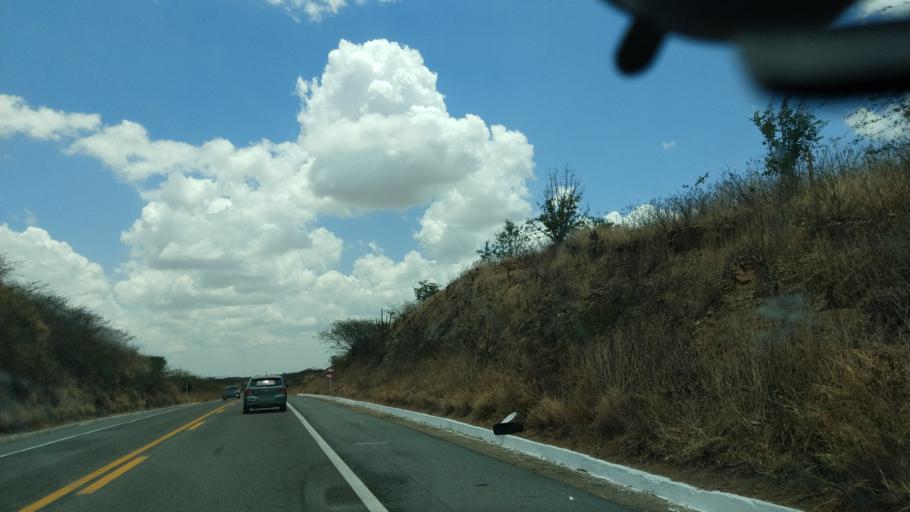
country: BR
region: Rio Grande do Norte
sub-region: Cerro Cora
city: Cerro Cora
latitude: -6.1997
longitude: -36.2710
